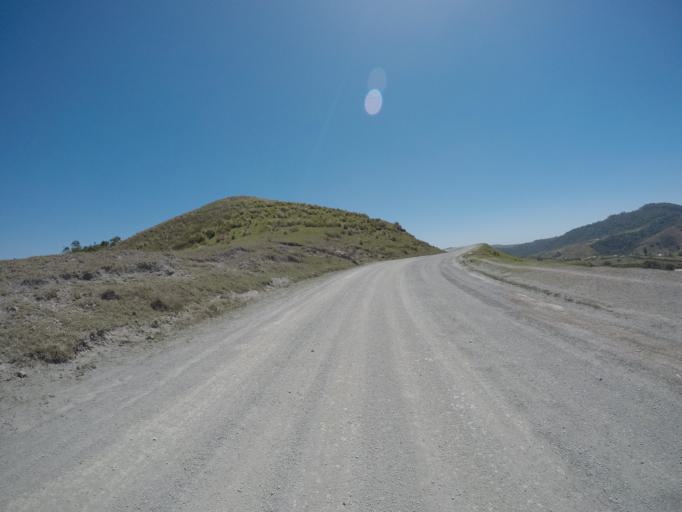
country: ZA
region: Eastern Cape
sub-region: OR Tambo District Municipality
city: Libode
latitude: -32.0154
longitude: 29.0774
